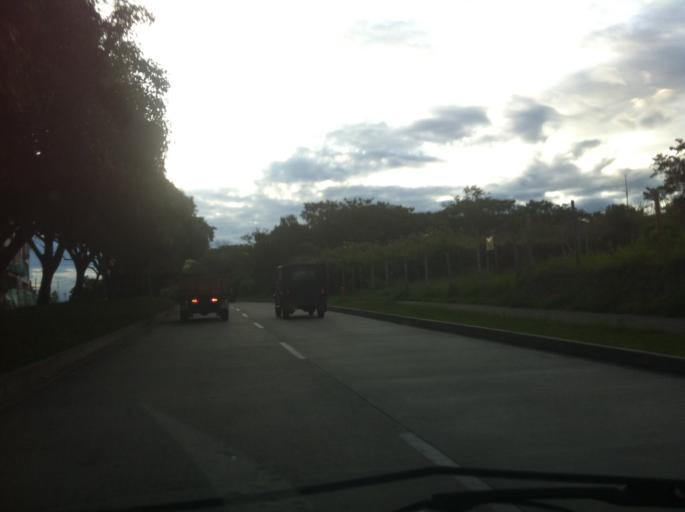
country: CO
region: Quindio
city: Armenia
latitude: 4.5583
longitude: -75.6597
